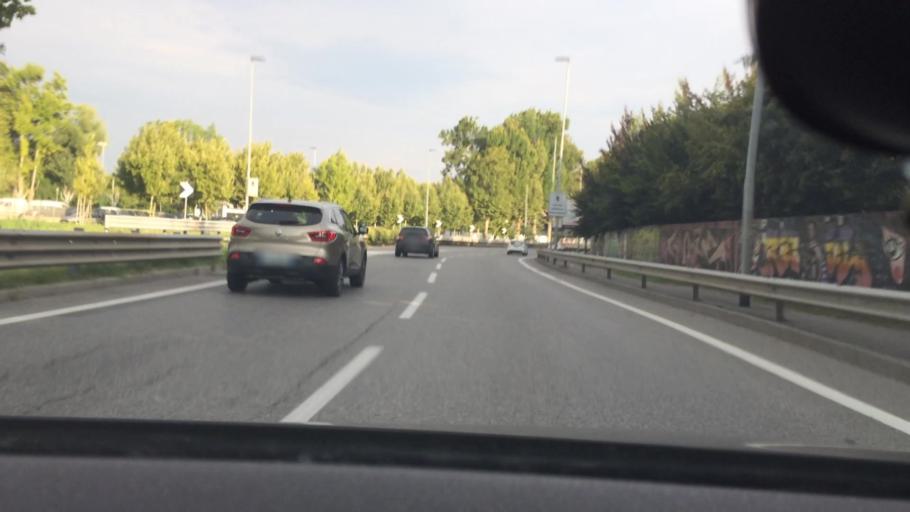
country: IT
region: Lombardy
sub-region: Provincia di Bergamo
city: Gorle
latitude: 45.7022
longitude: 9.6950
